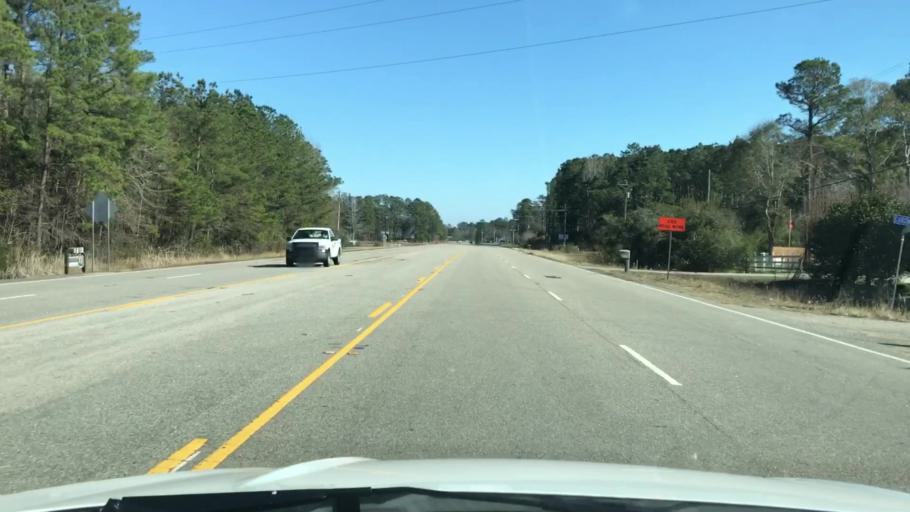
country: US
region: South Carolina
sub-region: Horry County
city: Garden City
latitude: 33.6297
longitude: -79.0306
